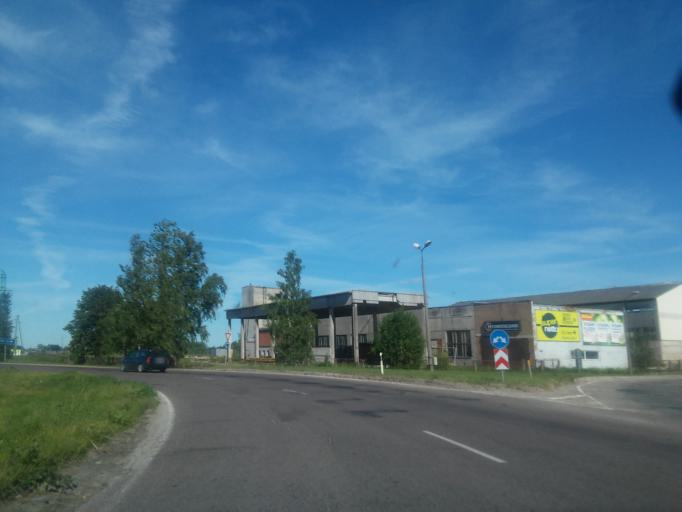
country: LV
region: Saldus Rajons
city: Saldus
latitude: 56.6815
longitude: 22.4728
